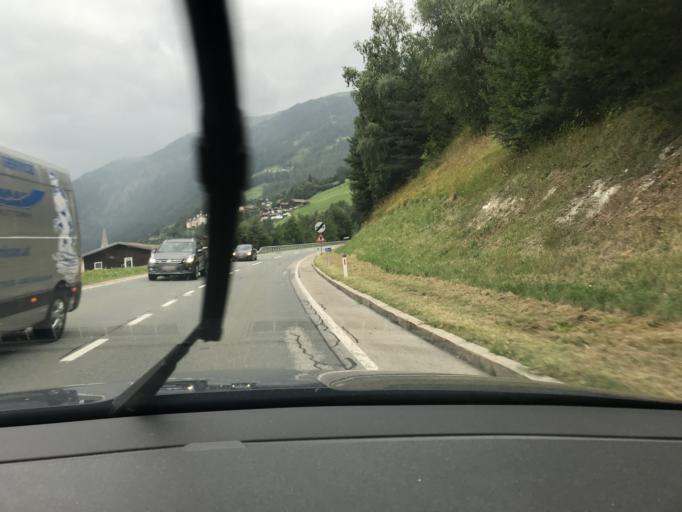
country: AT
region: Tyrol
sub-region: Politischer Bezirk Lienz
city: Matrei in Osttirol
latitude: 46.9930
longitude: 12.5431
